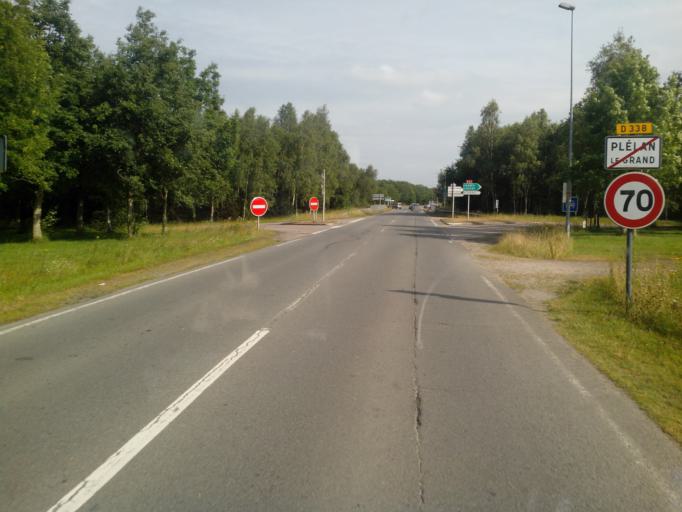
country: FR
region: Brittany
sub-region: Departement d'Ille-et-Vilaine
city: Plelan-le-Grand
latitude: 48.0052
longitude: -2.0869
